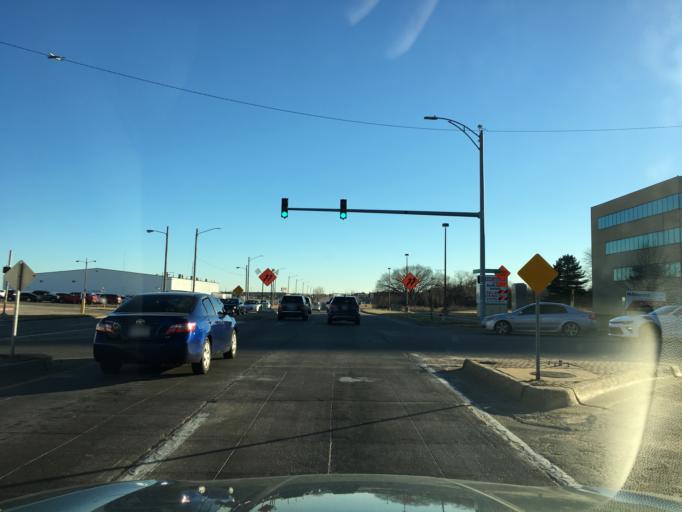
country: US
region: Kansas
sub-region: Sedgwick County
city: Bellaire
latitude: 37.6869
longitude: -97.2263
